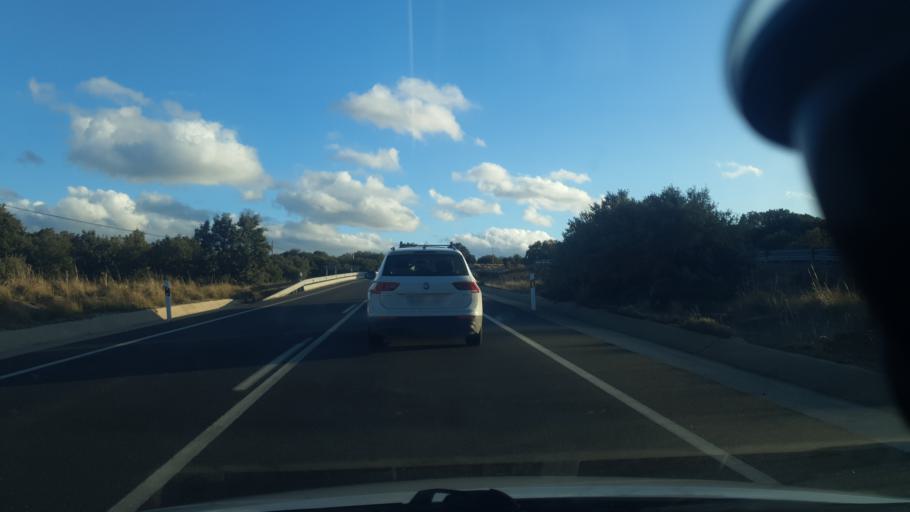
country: ES
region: Castille and Leon
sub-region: Provincia de Avila
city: Mingorria
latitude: 40.7212
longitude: -4.6733
